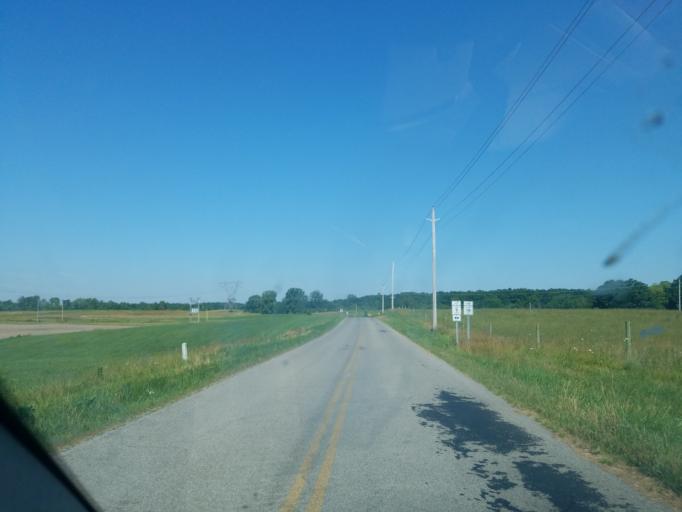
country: US
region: Ohio
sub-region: Logan County
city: Northwood
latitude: 40.4422
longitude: -83.6858
